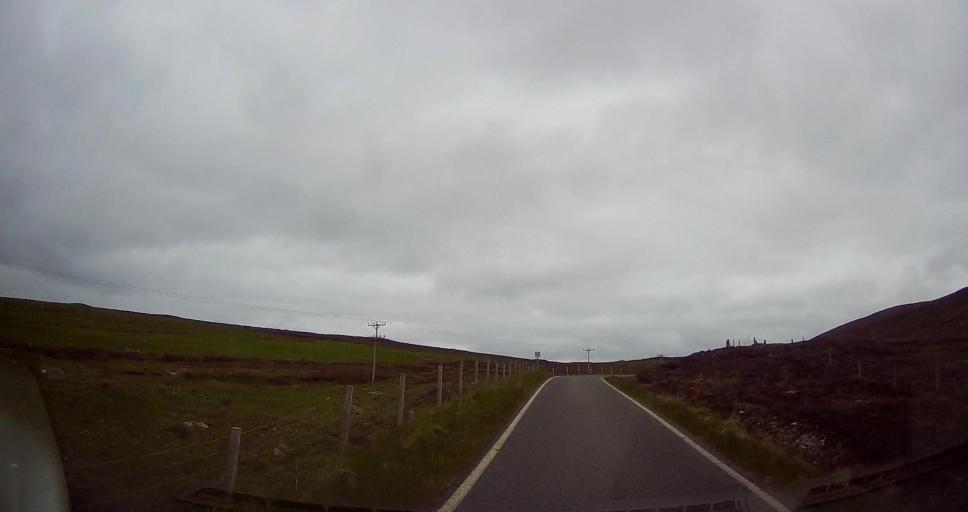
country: GB
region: Scotland
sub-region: Shetland Islands
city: Lerwick
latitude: 60.3070
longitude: -1.3378
